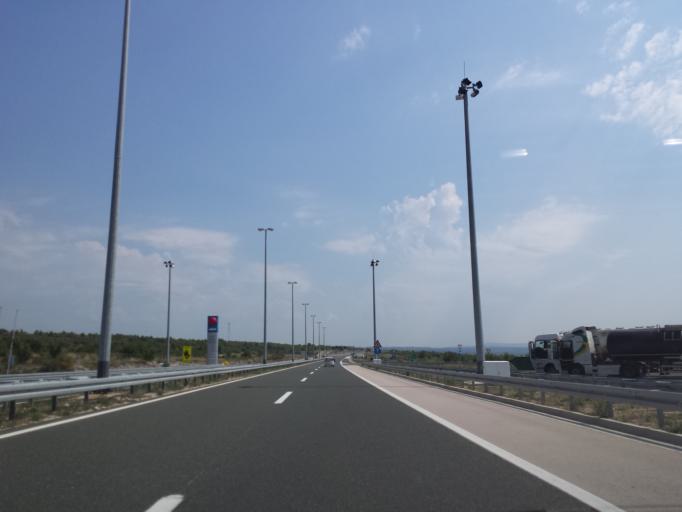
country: HR
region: Sibensko-Kniniska
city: Zaton
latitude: 43.8561
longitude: 15.8462
